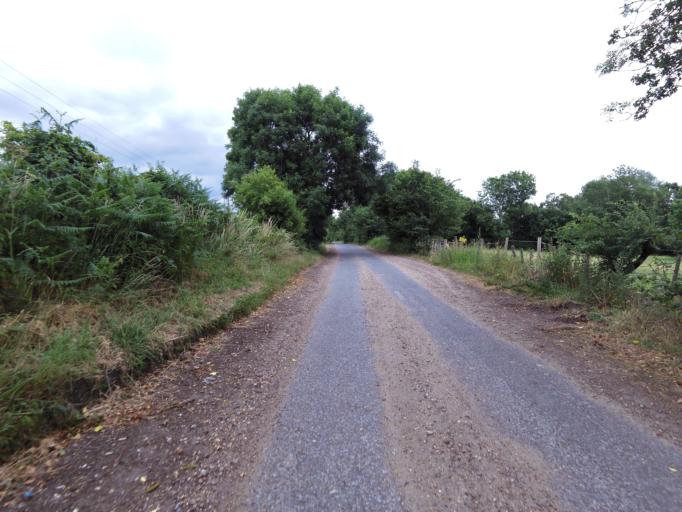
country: GB
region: England
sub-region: Suffolk
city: Bungay
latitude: 52.4372
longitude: 1.3889
